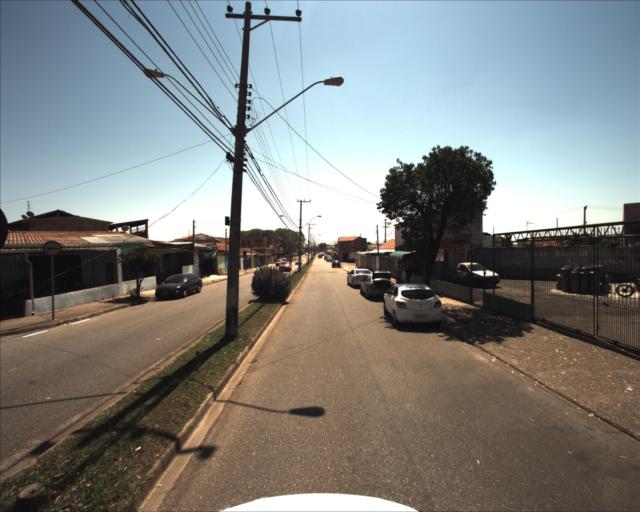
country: BR
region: Sao Paulo
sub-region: Sorocaba
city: Sorocaba
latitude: -23.4743
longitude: -47.4854
